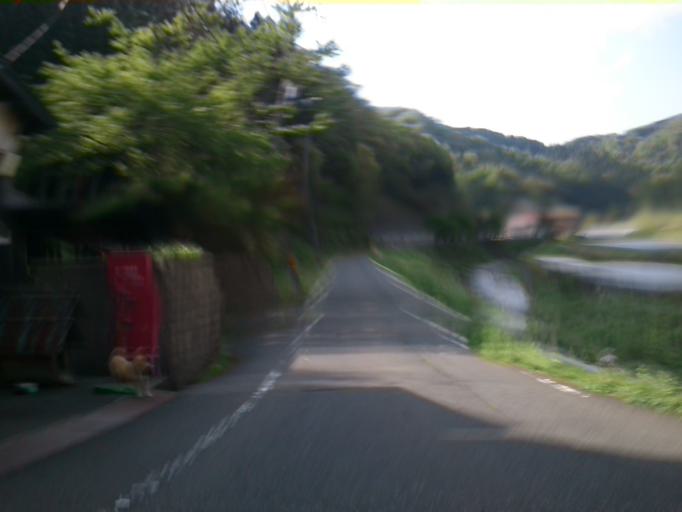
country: JP
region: Kyoto
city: Miyazu
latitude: 35.6821
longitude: 135.1580
